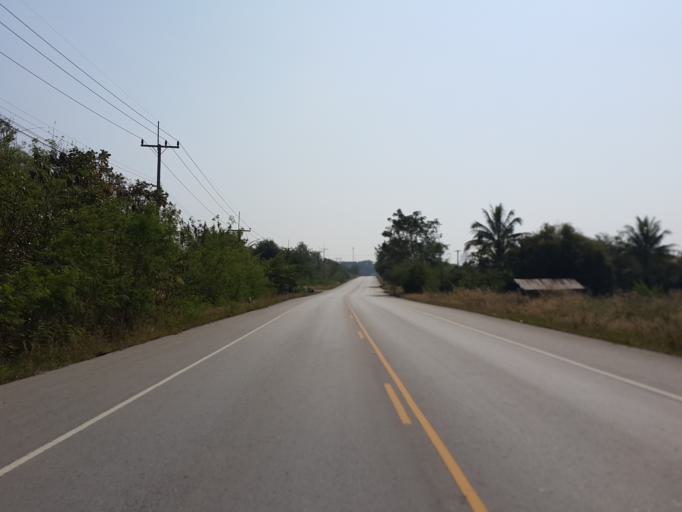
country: TH
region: Lampang
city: Mueang Pan
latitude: 18.9174
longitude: 99.6103
